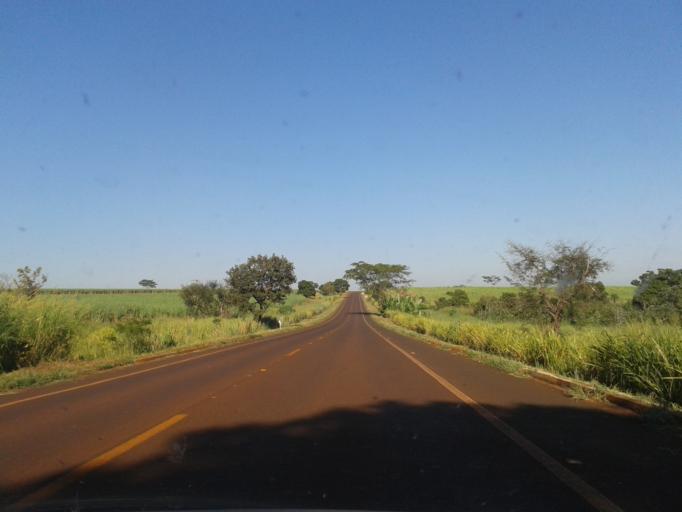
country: BR
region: Minas Gerais
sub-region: Capinopolis
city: Capinopolis
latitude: -18.6949
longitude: -49.6271
